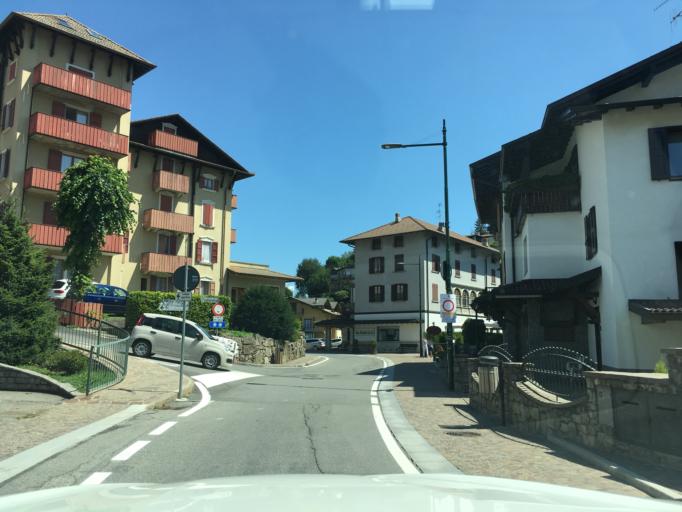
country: IT
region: Lombardy
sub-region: Provincia di Bergamo
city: Selvino
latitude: 45.7824
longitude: 9.7560
